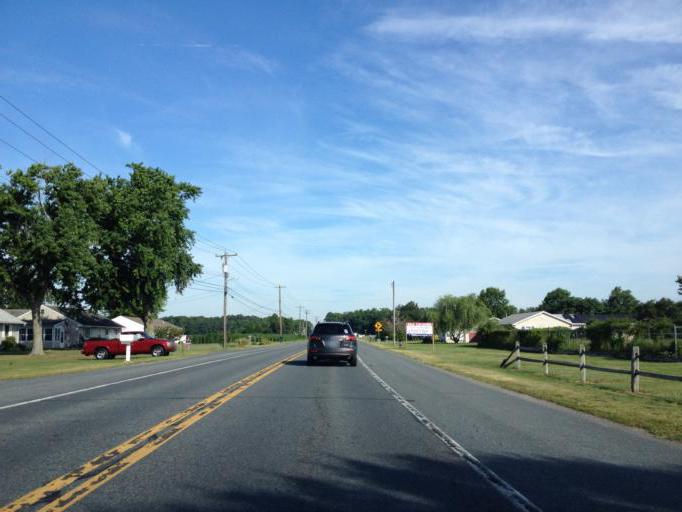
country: US
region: Delaware
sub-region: Sussex County
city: Millsboro
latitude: 38.5562
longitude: -75.2562
